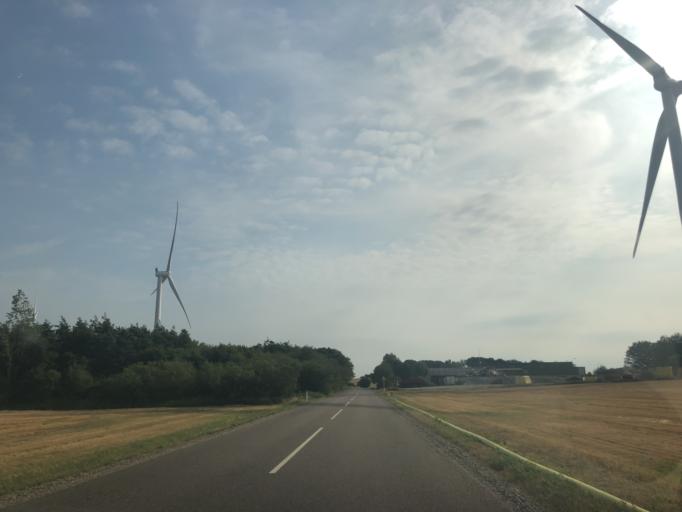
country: DK
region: Central Jutland
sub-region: Skive Kommune
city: Skive
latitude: 56.6838
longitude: 8.9721
